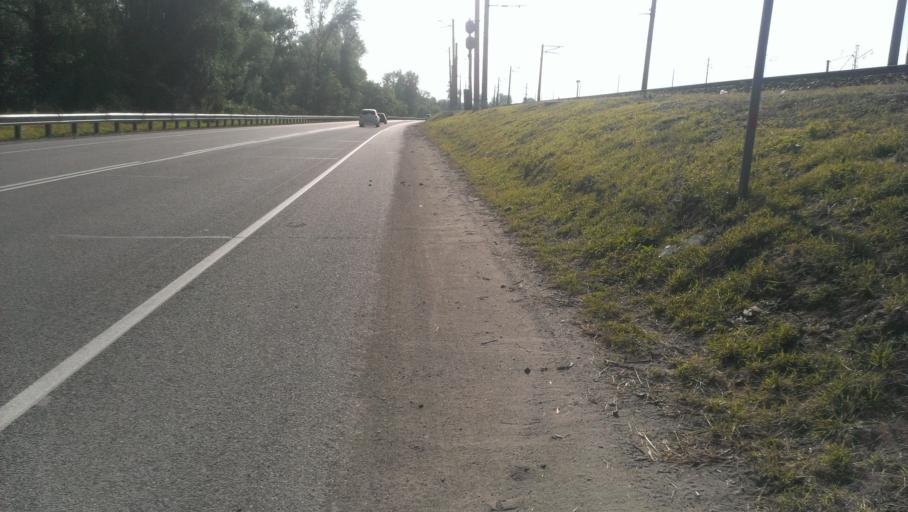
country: RU
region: Altai Krai
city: Zaton
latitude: 53.3676
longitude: 83.8506
